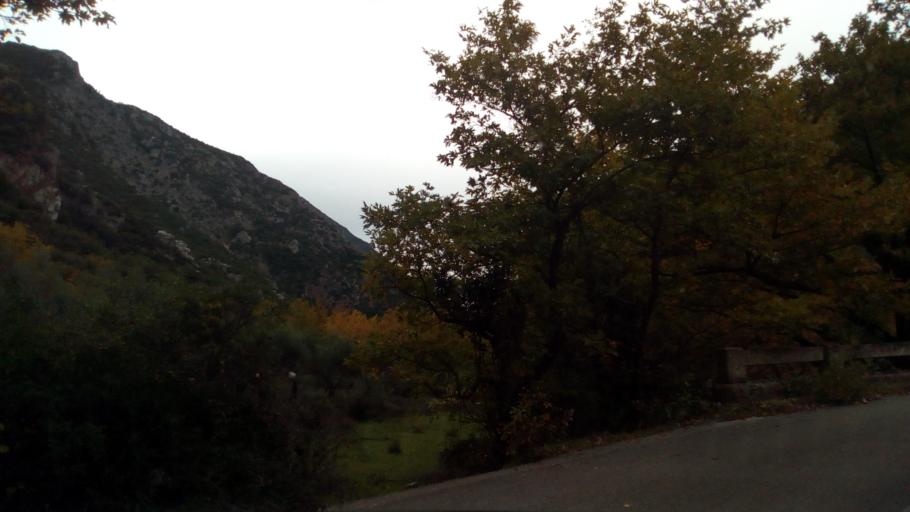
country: GR
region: West Greece
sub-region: Nomos Aitolias kai Akarnanias
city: Thermo
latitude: 38.5976
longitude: 21.8526
